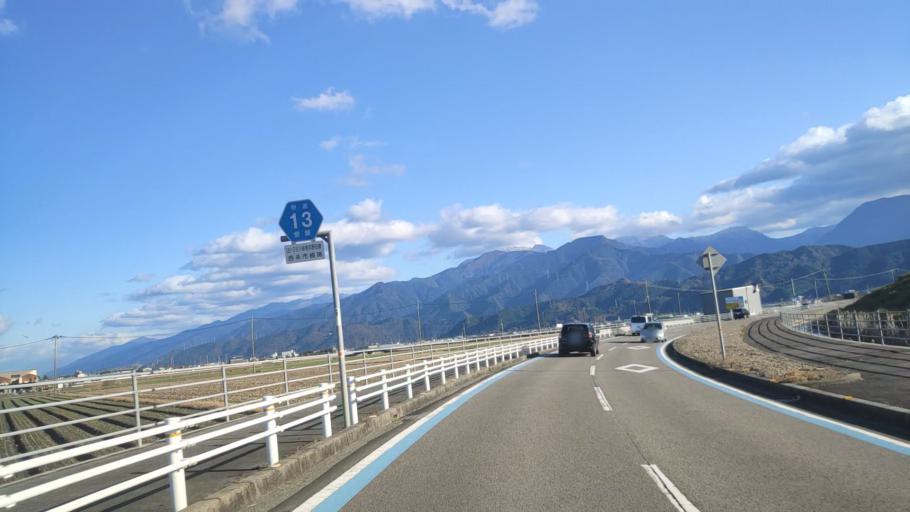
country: JP
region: Ehime
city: Saijo
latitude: 33.9091
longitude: 133.1414
